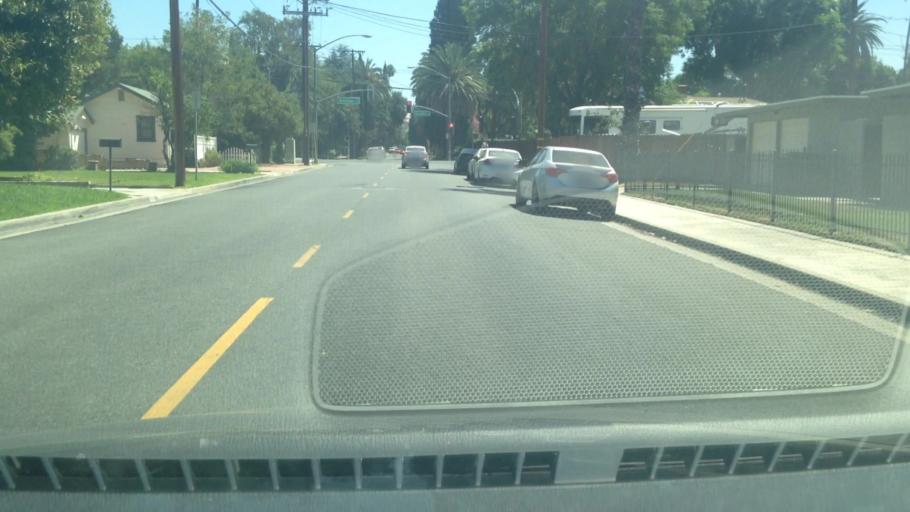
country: US
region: California
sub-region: Riverside County
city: Riverside
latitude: 33.9683
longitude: -117.3931
